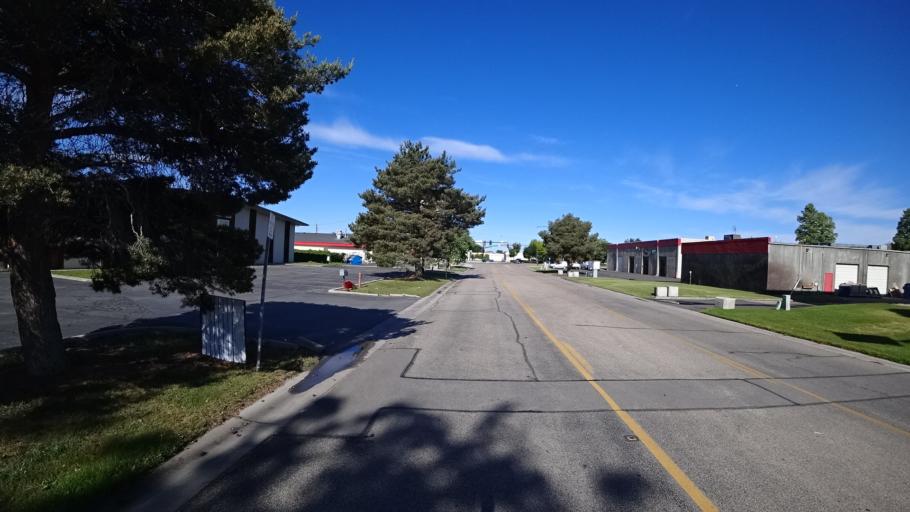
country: US
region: Idaho
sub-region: Ada County
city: Garden City
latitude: 43.5839
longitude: -116.2728
